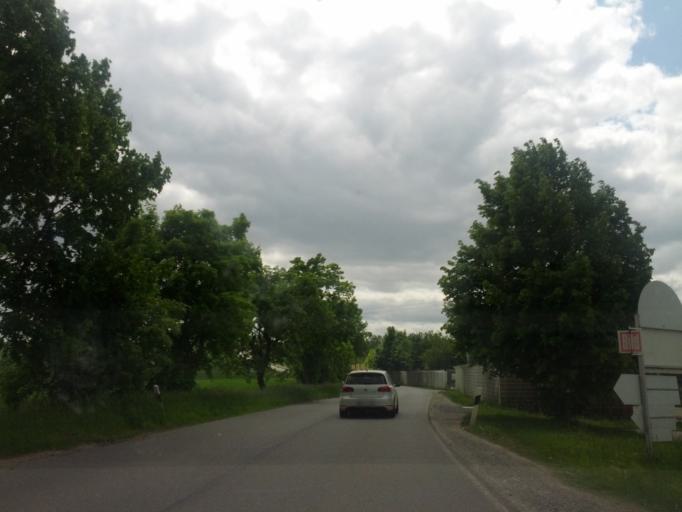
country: DE
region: Saxony
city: Bannewitz
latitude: 51.0014
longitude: 13.7639
